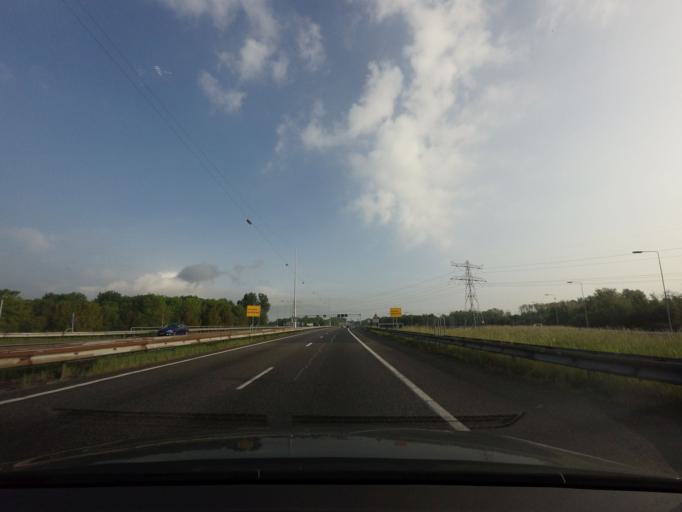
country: NL
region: North Holland
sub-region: Gemeente Velsen
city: Velsen-Zuid
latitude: 52.4511
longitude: 4.6587
